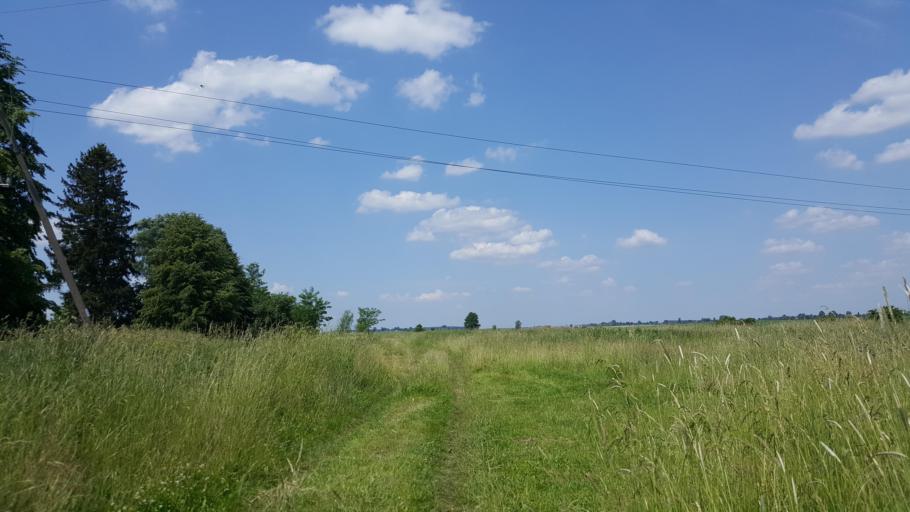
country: BY
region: Brest
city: Kamyanyets
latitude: 52.4080
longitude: 23.7744
